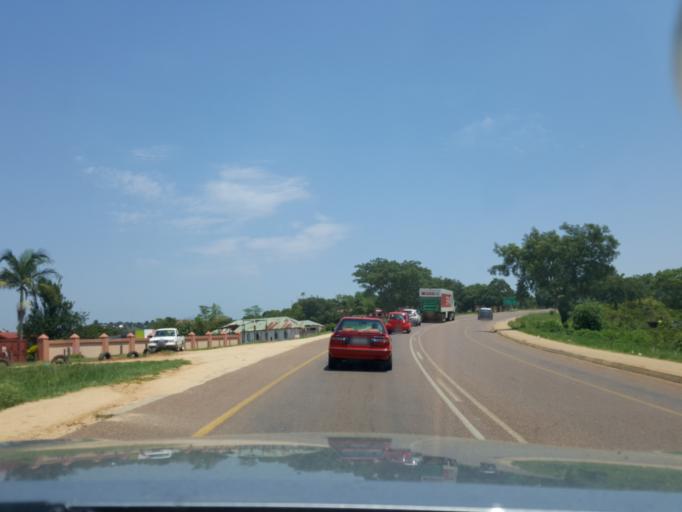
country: ZA
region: Limpopo
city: Thulamahashi
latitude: -24.9503
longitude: 31.1263
